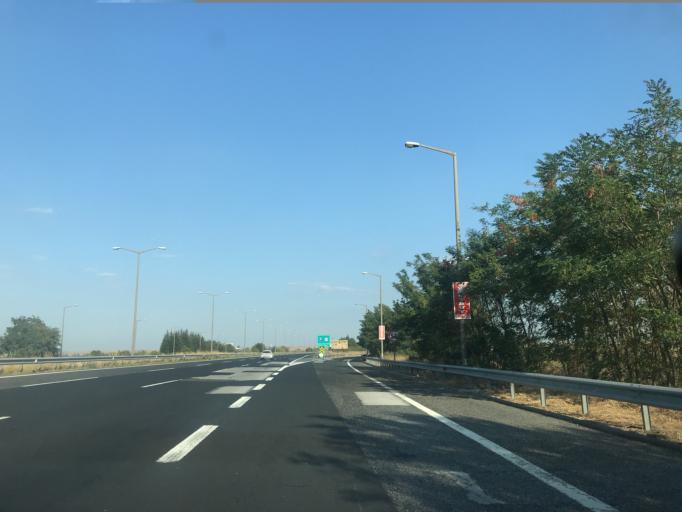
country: TR
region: Kirklareli
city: Buyukkaristiran
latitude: 41.3865
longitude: 27.5579
